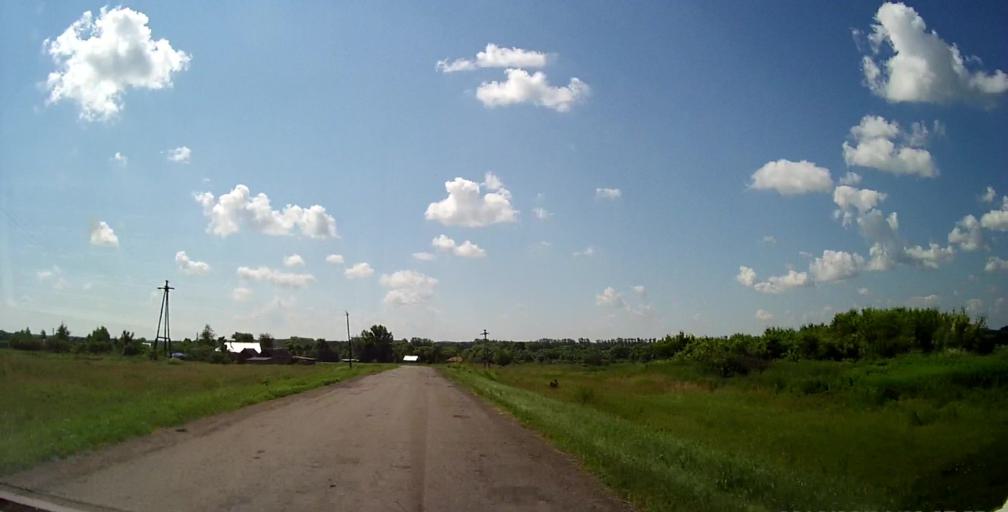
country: RU
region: Lipetsk
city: Chaplygin
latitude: 53.3543
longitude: 39.9250
